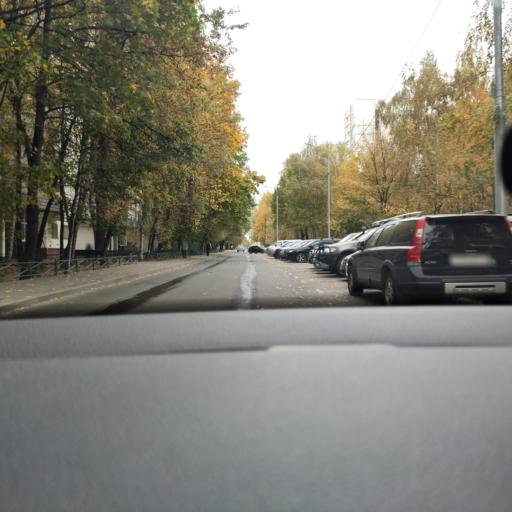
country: RU
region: Moscow
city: Lianozovo
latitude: 55.8945
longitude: 37.5768
